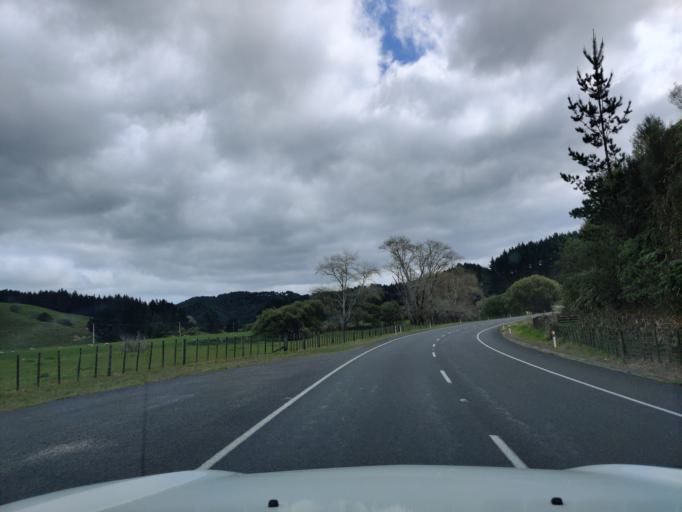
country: NZ
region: Manawatu-Wanganui
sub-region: Wanganui District
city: Wanganui
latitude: -39.8485
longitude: 175.1352
